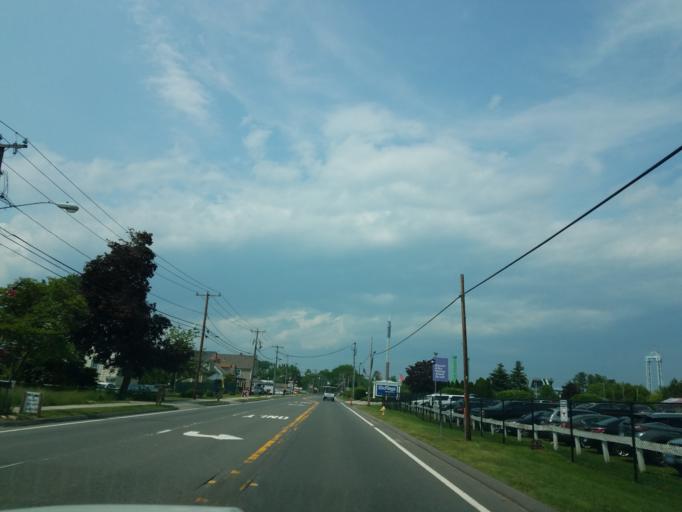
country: US
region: Massachusetts
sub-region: Hampden County
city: Agawam
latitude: 42.0343
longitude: -72.6167
